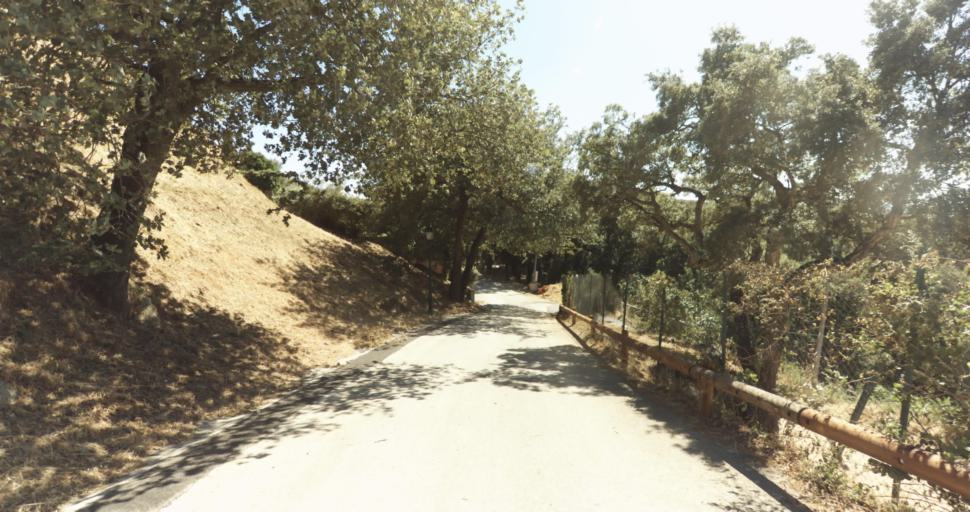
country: FR
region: Provence-Alpes-Cote d'Azur
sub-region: Departement du Var
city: Gassin
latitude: 43.2322
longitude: 6.5847
